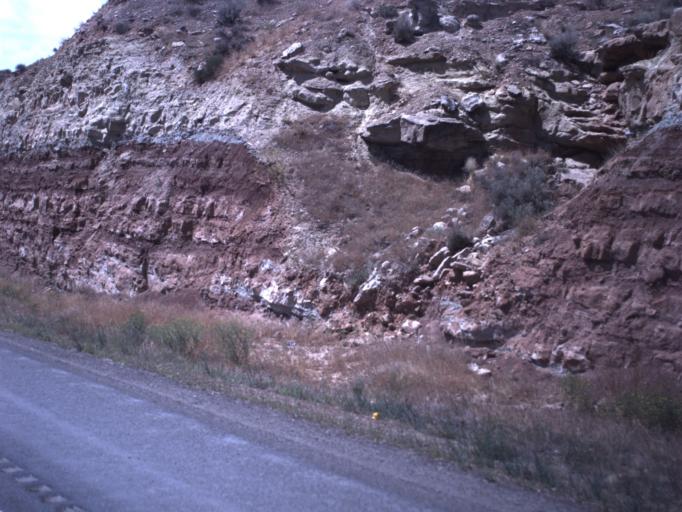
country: US
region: Utah
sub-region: Uintah County
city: Maeser
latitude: 40.3465
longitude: -109.6261
